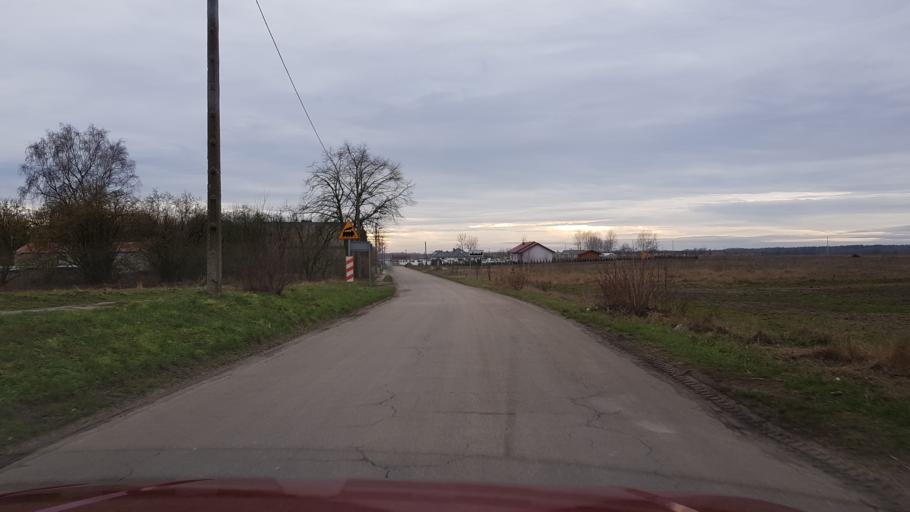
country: PL
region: West Pomeranian Voivodeship
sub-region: Powiat policki
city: Police
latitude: 53.5906
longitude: 14.5338
